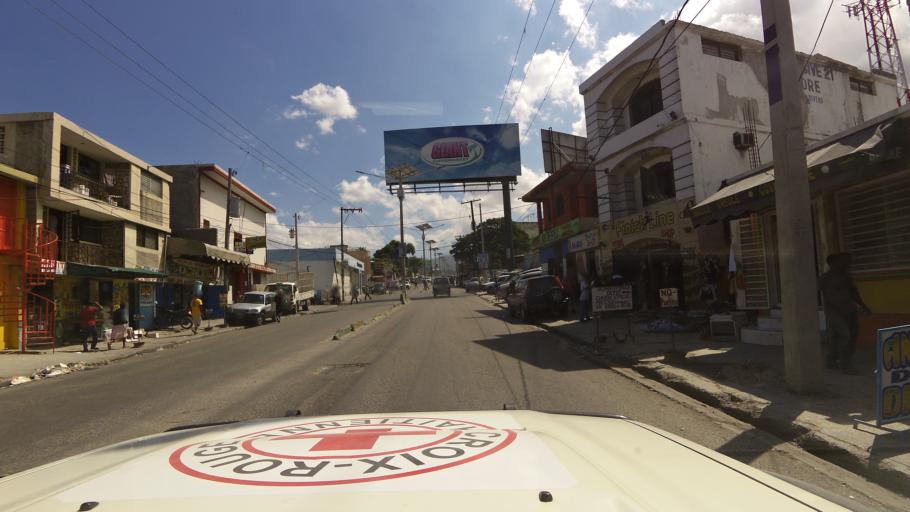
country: HT
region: Ouest
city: Delmas 73
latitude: 18.5418
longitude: -72.2986
